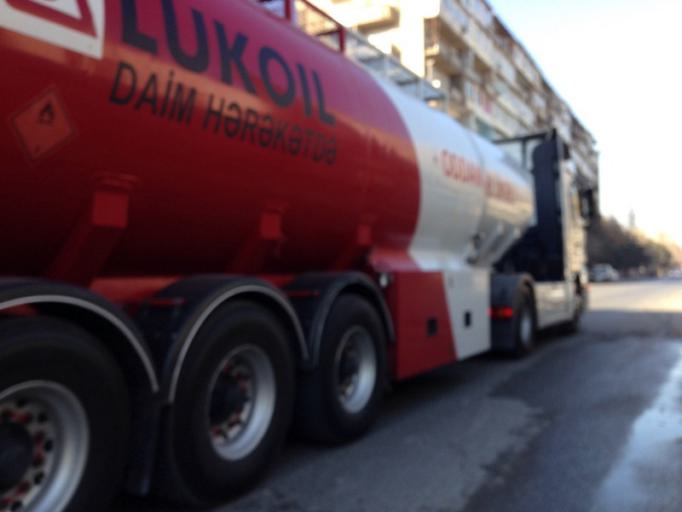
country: AZ
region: Baki
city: Baku
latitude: 40.4083
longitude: 49.8742
